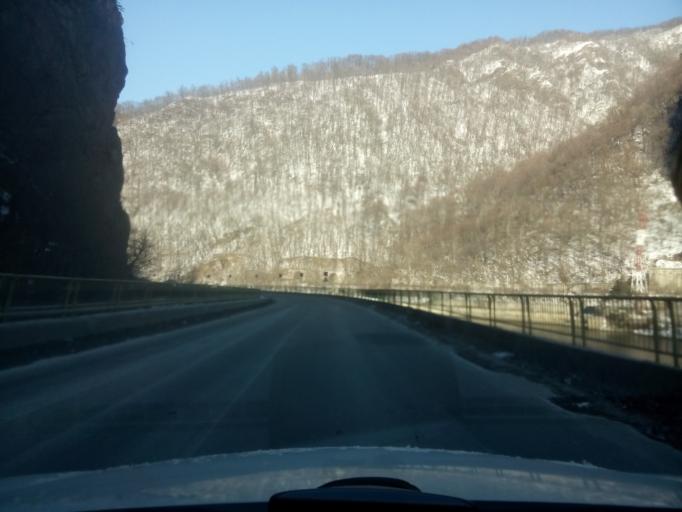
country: RO
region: Valcea
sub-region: Comuna Brezoi
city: Brezoi
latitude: 45.2969
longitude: 24.2907
